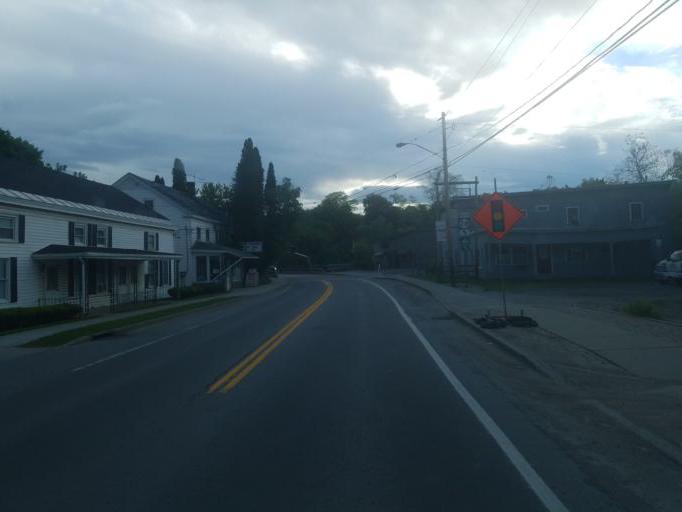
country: US
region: New York
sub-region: Herkimer County
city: Herkimer
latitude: 43.1377
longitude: -74.9713
